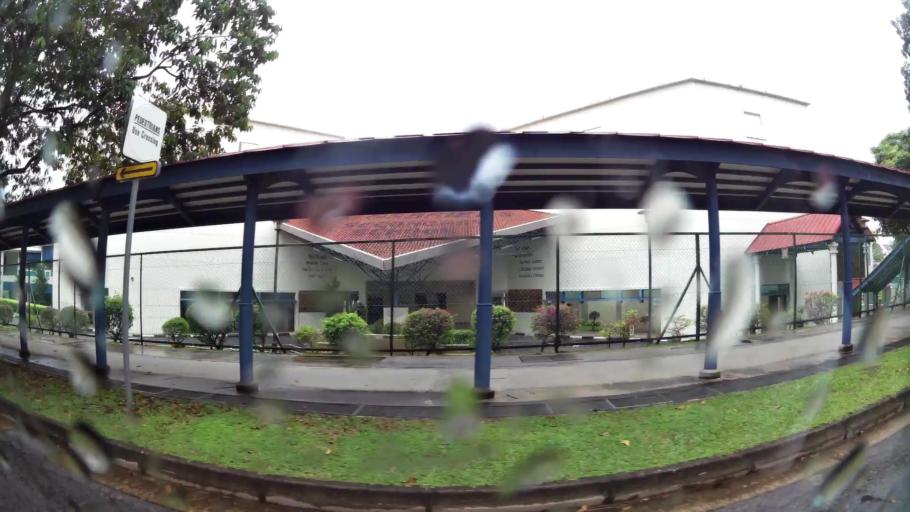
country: SG
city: Singapore
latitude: 1.3476
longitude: 103.8757
